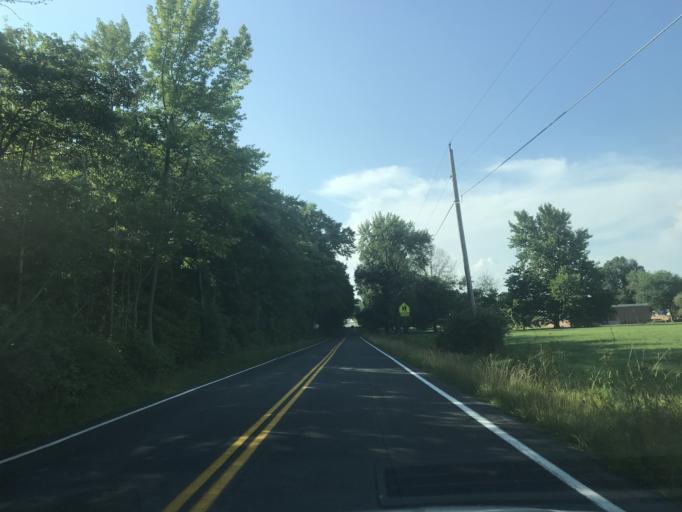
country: US
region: Maryland
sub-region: Harford County
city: Aberdeen
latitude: 39.5194
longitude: -76.1354
